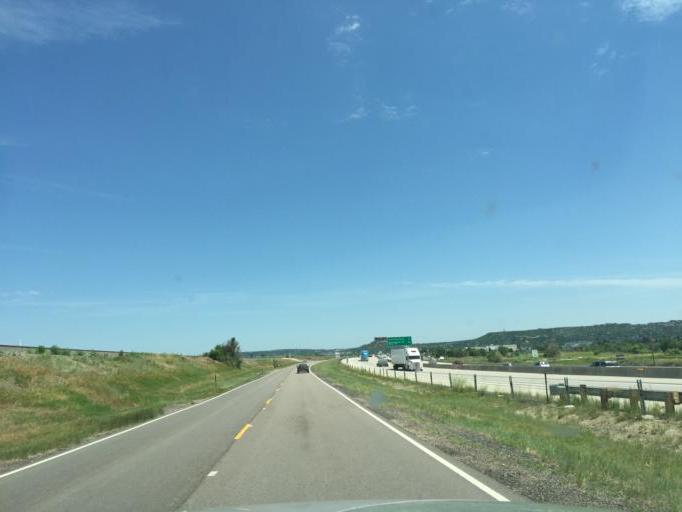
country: US
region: Colorado
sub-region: Douglas County
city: Castle Rock
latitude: 39.3498
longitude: -104.8724
